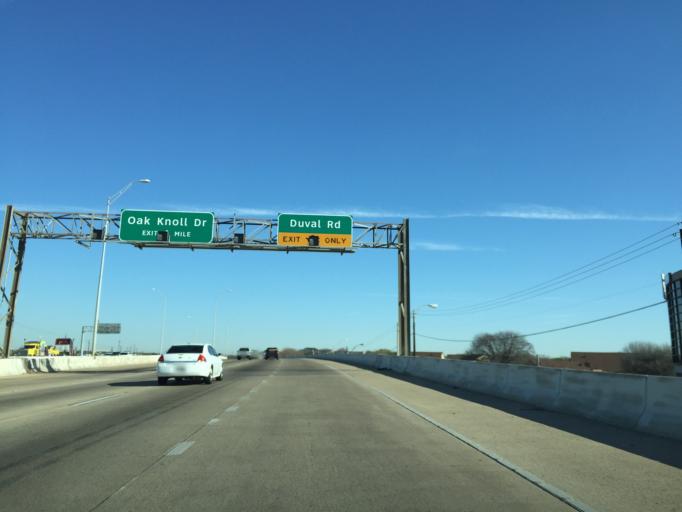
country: US
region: Texas
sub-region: Williamson County
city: Jollyville
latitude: 30.4069
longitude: -97.7450
